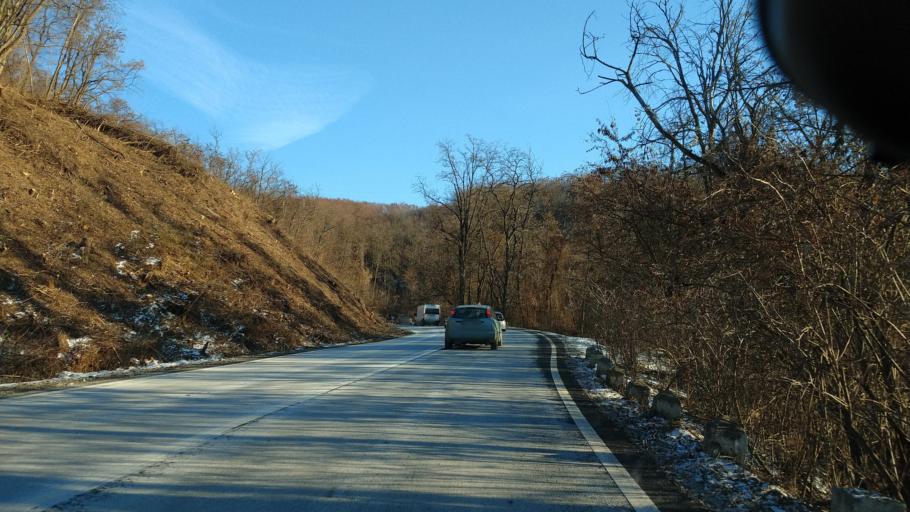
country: RO
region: Bacau
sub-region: Comuna Luizi-Calugara
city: Luizi-Calugara
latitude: 46.5431
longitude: 26.8190
